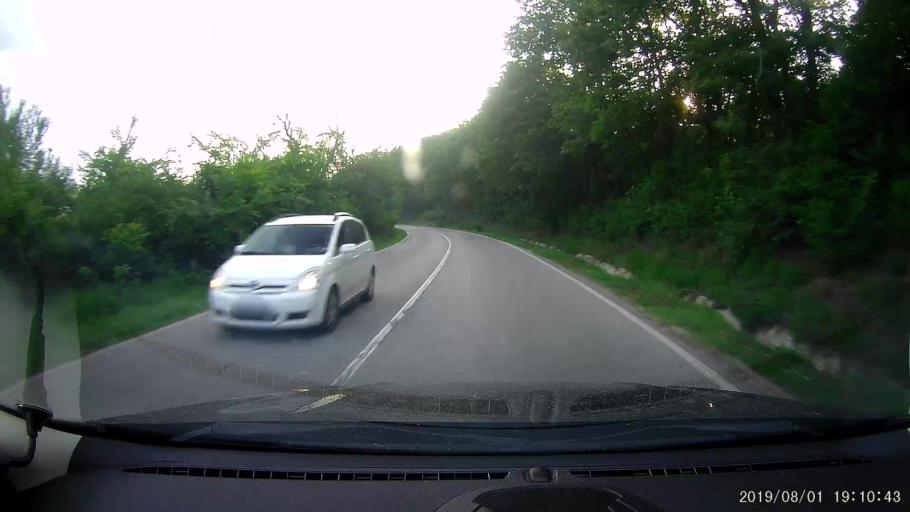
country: BG
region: Shumen
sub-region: Obshtina Smyadovo
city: Smyadovo
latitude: 42.9787
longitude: 26.9730
